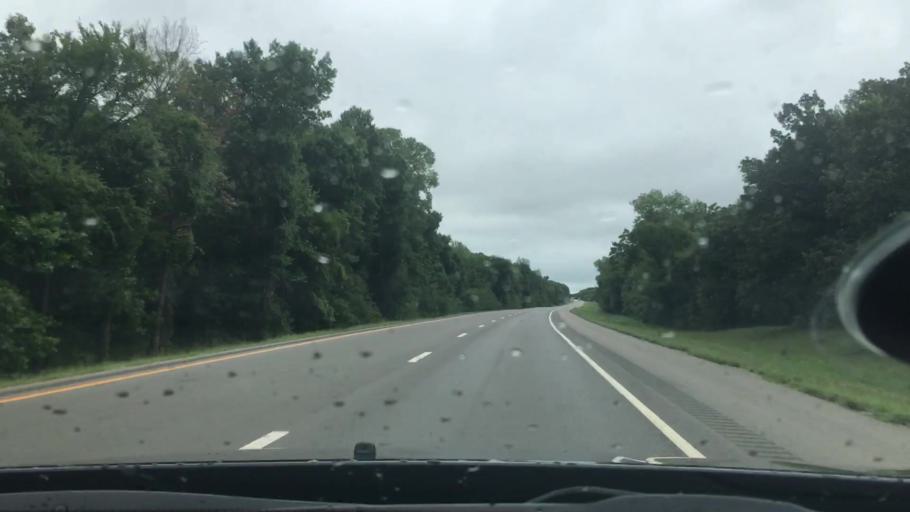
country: US
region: Oklahoma
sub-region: Okmulgee County
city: Morris
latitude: 35.4495
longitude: -95.7517
